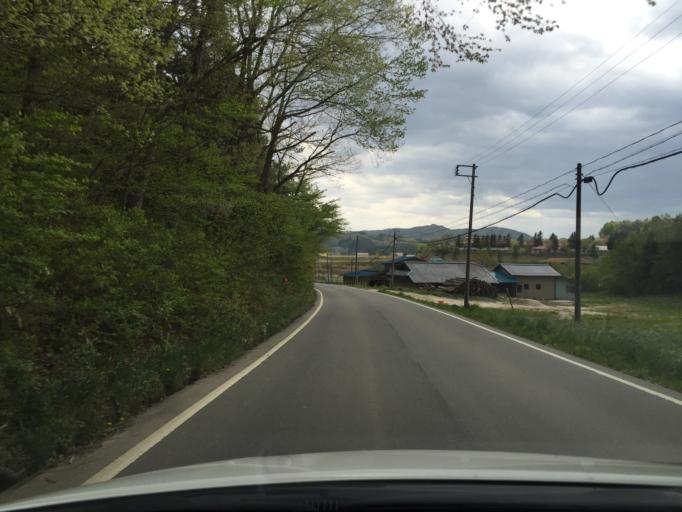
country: JP
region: Fukushima
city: Yanagawamachi-saiwaicho
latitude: 37.7032
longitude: 140.7483
